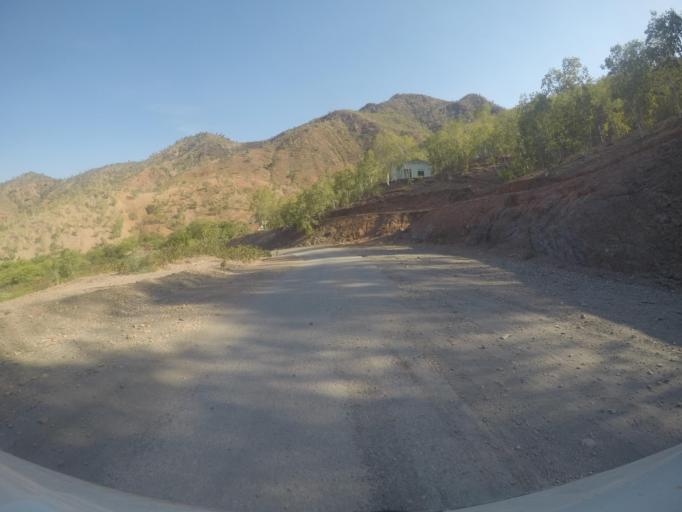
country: TL
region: Dili
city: Dili
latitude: -8.5272
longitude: 125.6308
